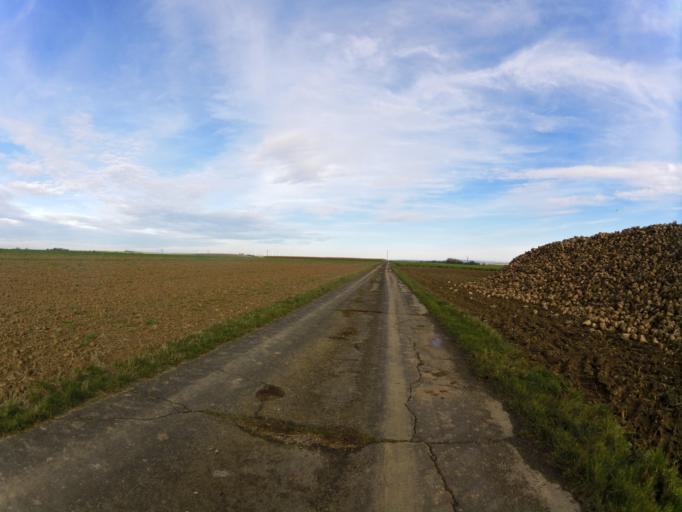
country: DE
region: Bavaria
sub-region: Regierungsbezirk Unterfranken
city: Giebelstadt
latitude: 49.6614
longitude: 9.9734
